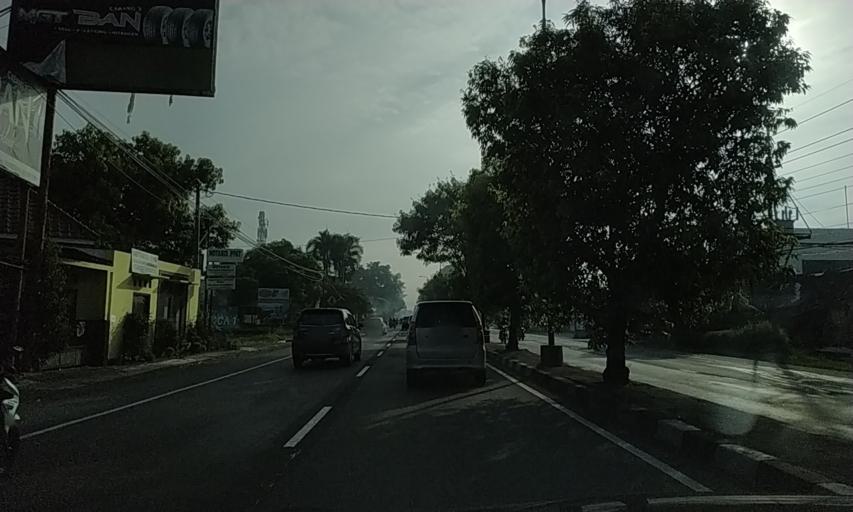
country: ID
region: Central Java
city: Candi Prambanan
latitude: -7.7652
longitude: 110.4731
